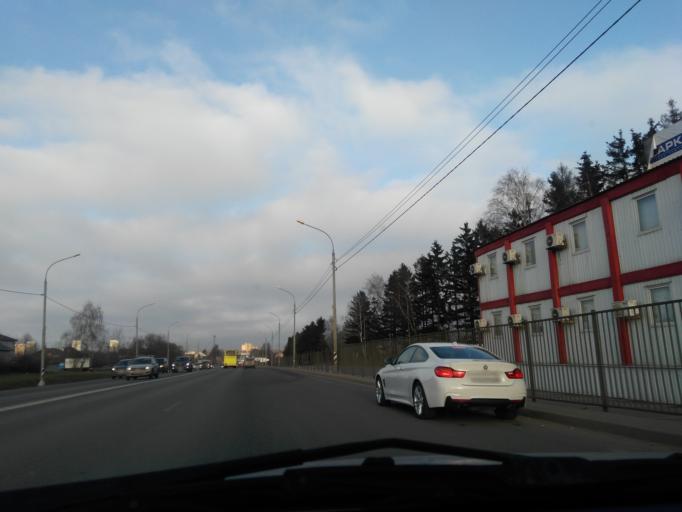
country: RU
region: Moskovskaya
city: Vatutinki
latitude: 55.4879
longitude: 37.3246
